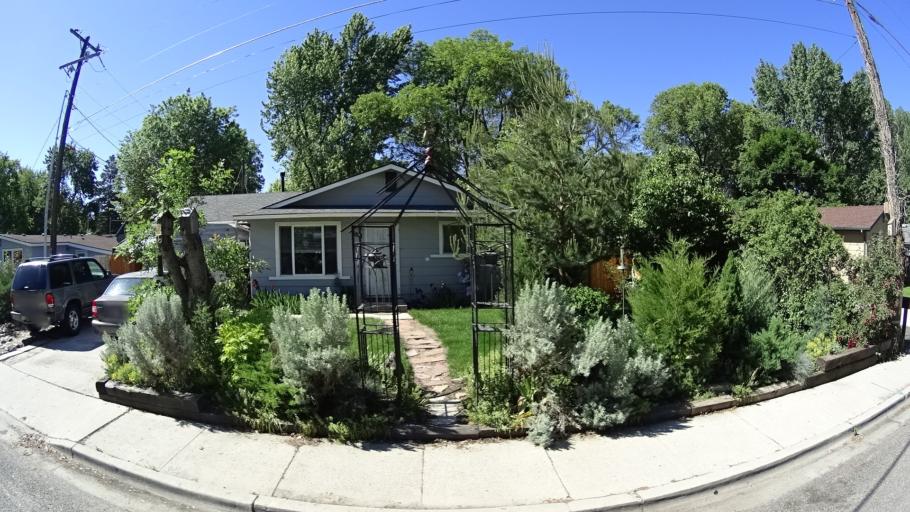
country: US
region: Idaho
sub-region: Ada County
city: Garden City
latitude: 43.6482
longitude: -116.2362
